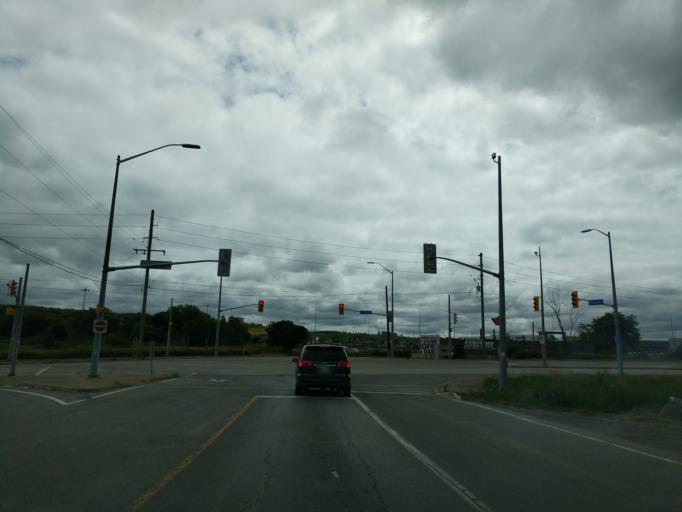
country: CA
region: Ontario
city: Thorold
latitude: 43.1605
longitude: -79.1681
